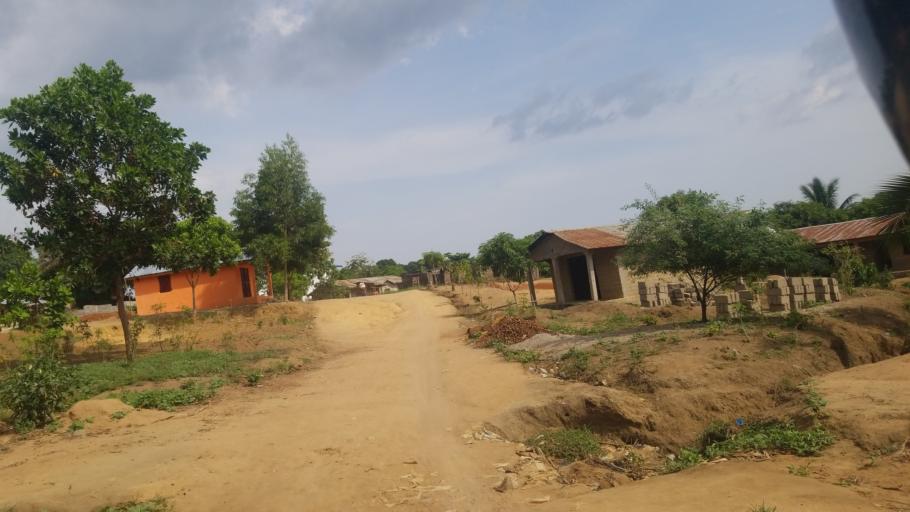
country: SL
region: Western Area
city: Waterloo
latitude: 8.3170
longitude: -13.0488
